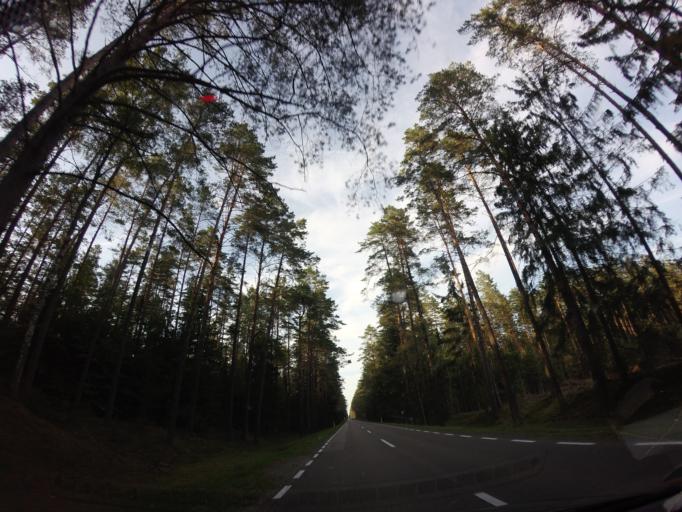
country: PL
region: Podlasie
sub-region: Powiat augustowski
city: Augustow
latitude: 53.8883
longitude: 23.1156
